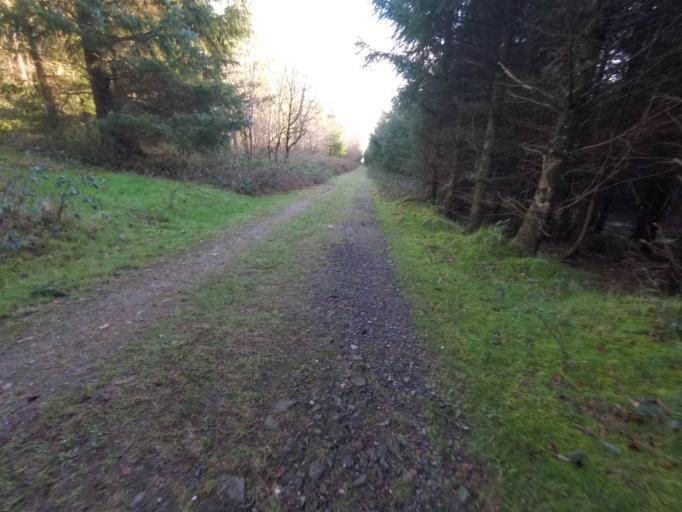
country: IE
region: Munster
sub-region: Waterford
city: Portlaw
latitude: 52.3083
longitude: -7.3563
